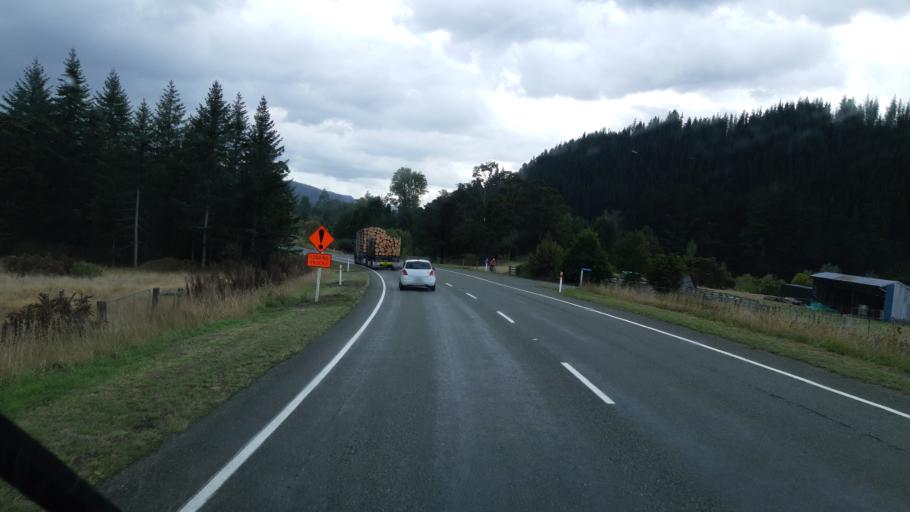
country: NZ
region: Tasman
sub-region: Tasman District
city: Wakefield
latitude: -41.4618
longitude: 172.9511
